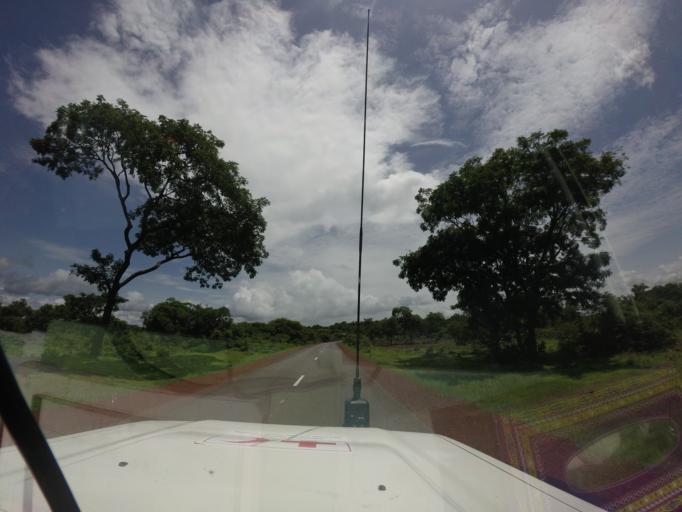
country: GN
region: Faranah
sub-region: Faranah Prefecture
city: Faranah
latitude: 10.0123
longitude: -10.8662
